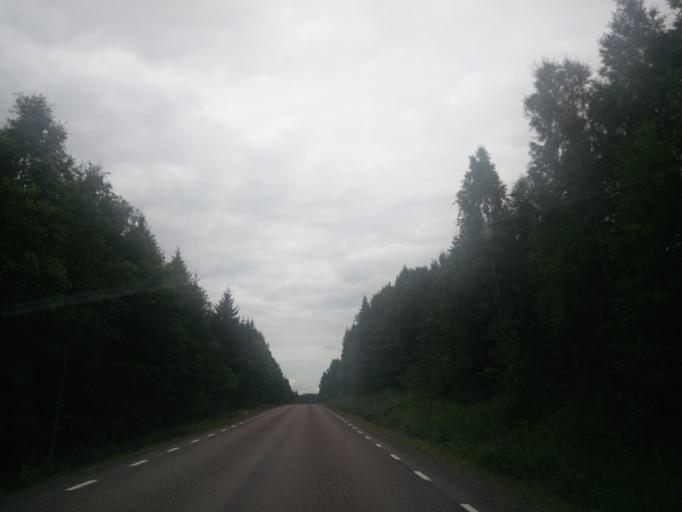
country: SE
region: Vaermland
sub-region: Torsby Kommun
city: Torsby
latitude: 59.9422
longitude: 12.7441
